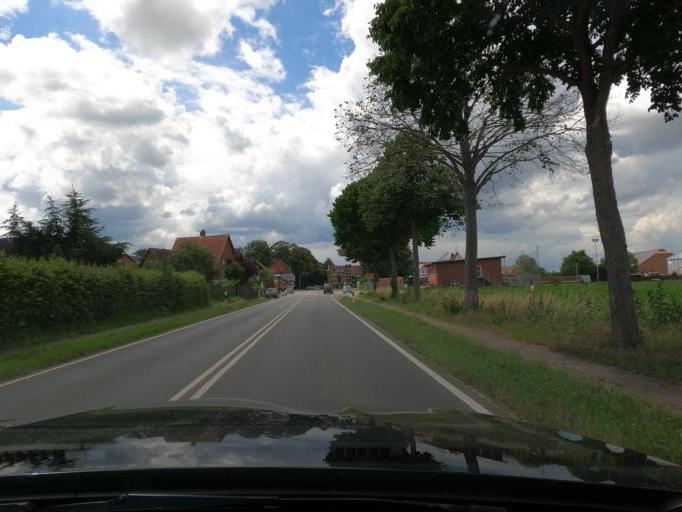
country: DE
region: Lower Saxony
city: Schellerten
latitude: 52.1728
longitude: 10.0417
